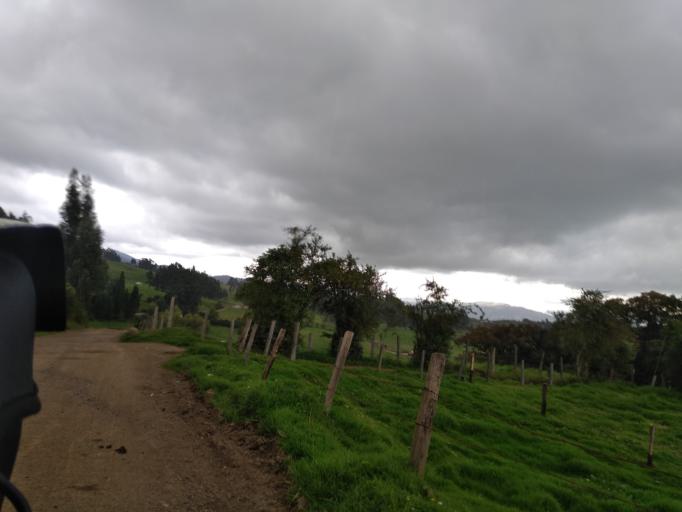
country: CO
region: Boyaca
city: Sotaquira
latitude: 5.7605
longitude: -73.2795
